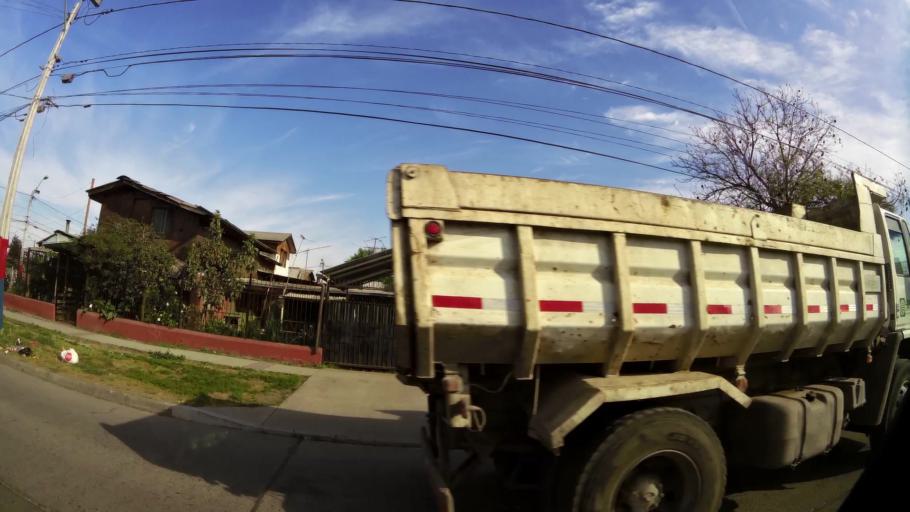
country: CL
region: Santiago Metropolitan
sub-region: Provincia de Talagante
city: Talagante
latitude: -33.6710
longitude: -70.9362
